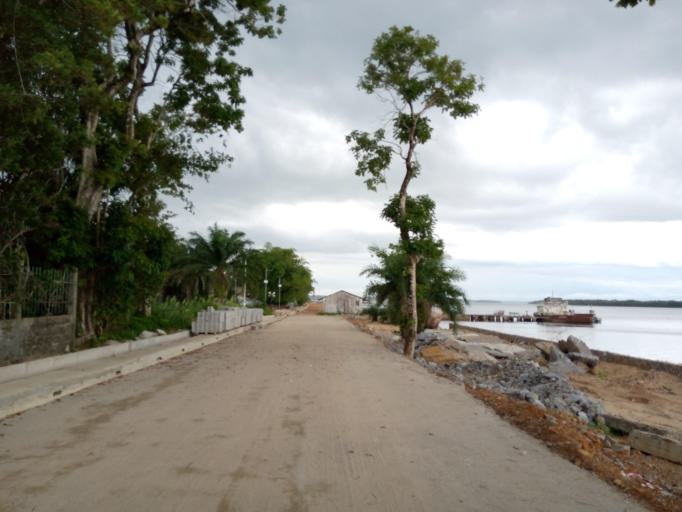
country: SL
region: Southern Province
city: Bonthe
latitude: 7.5257
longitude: -12.5001
